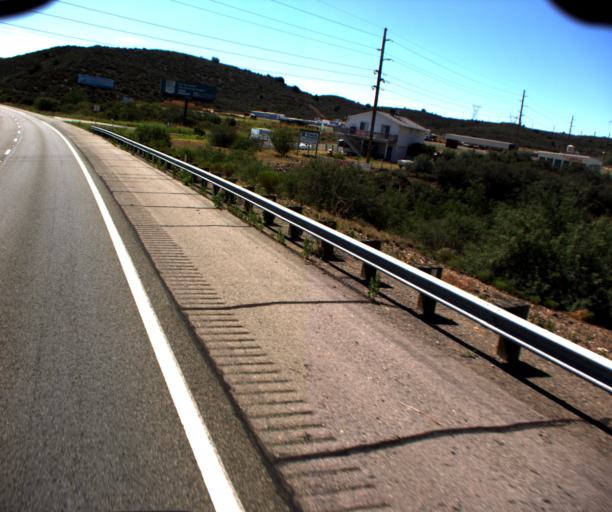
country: US
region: Arizona
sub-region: Yavapai County
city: Mayer
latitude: 34.3854
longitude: -112.2172
